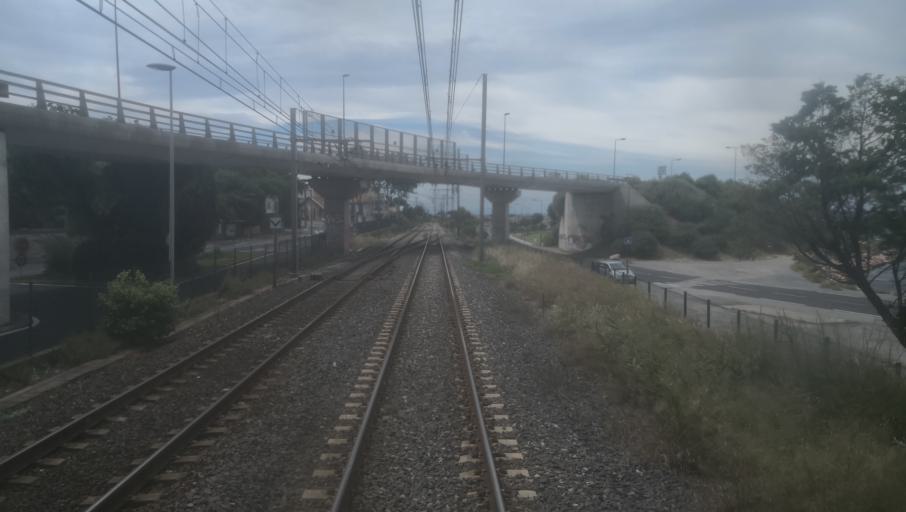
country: FR
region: Languedoc-Roussillon
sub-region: Departement de l'Herault
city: Sete
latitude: 43.4127
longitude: 3.6855
